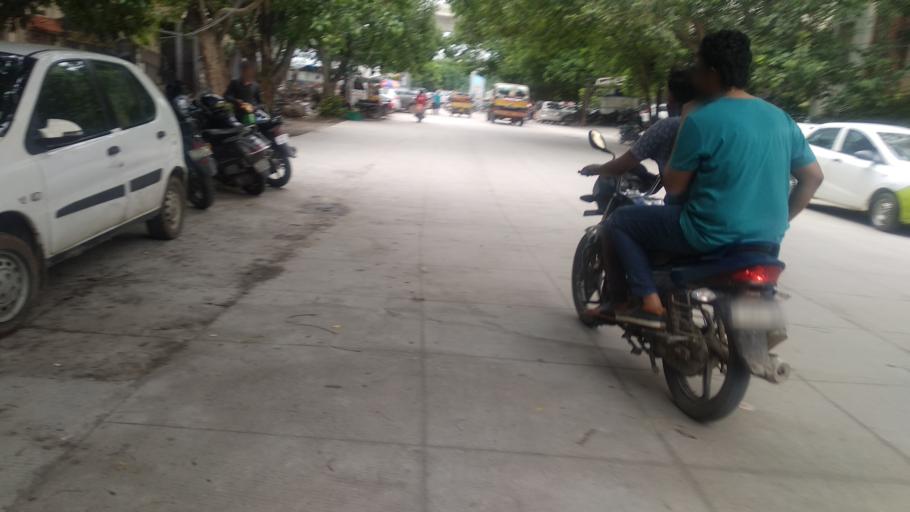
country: IN
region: Telangana
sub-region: Rangareddi
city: Kukatpalli
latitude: 17.4455
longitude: 78.3846
